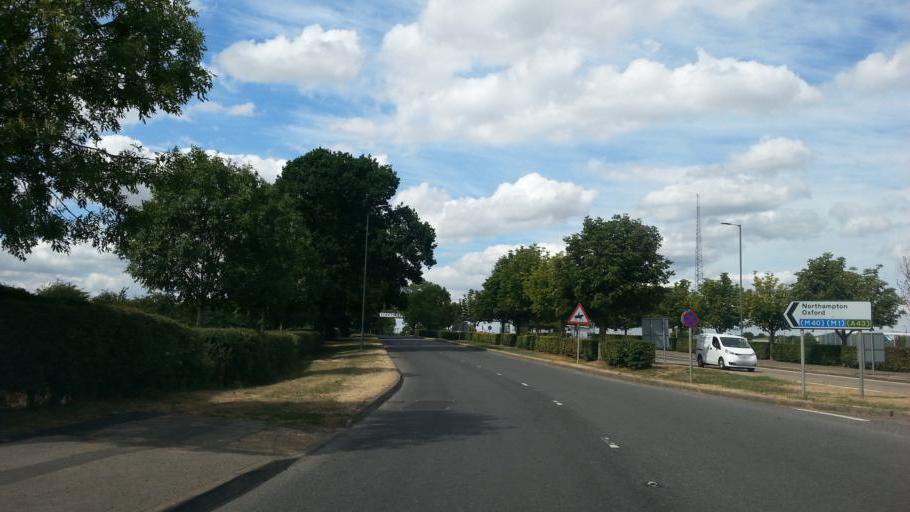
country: GB
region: England
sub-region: Northamptonshire
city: Silverstone
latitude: 52.0736
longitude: -1.0263
